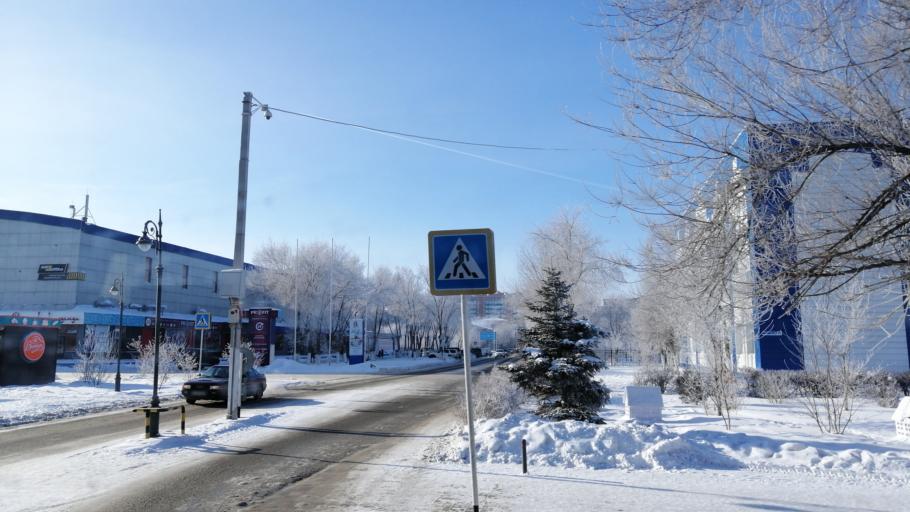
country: KZ
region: Aqtoebe
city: Aqtobe
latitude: 50.2950
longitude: 57.1584
